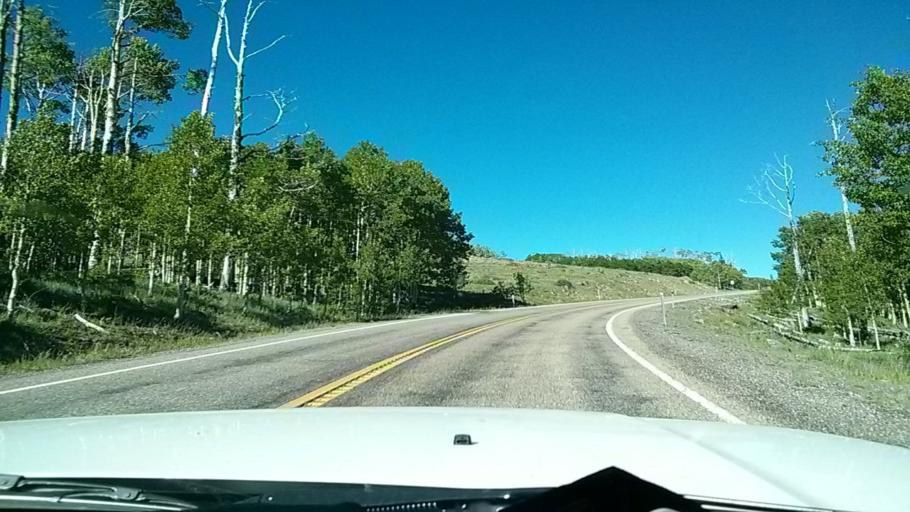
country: US
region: Utah
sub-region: Wayne County
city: Loa
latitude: 38.0330
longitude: -111.3369
